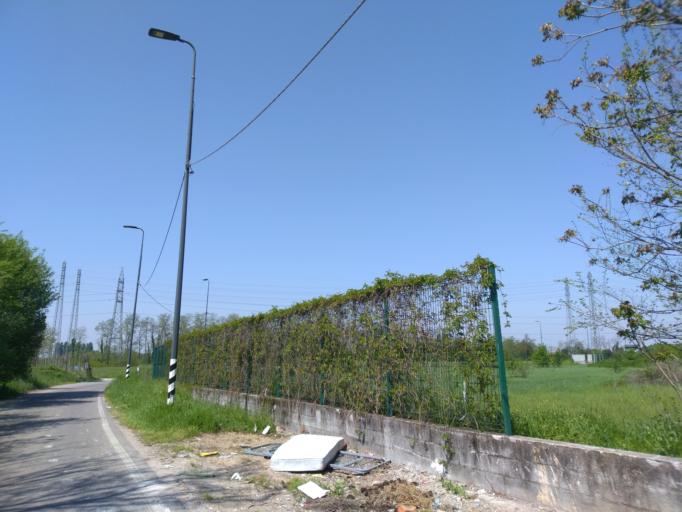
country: IT
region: Lombardy
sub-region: Citta metropolitana di Milano
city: Figino
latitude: 45.4822
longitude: 9.0851
